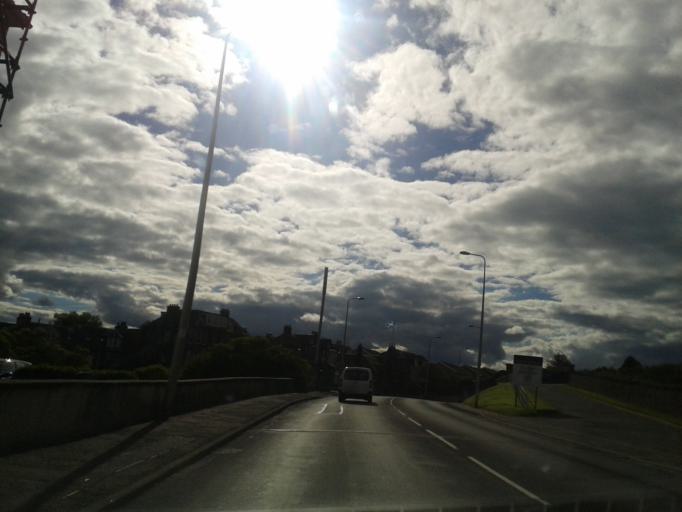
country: GB
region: Scotland
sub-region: Fife
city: Kinghorn
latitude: 56.0672
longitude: -3.1783
